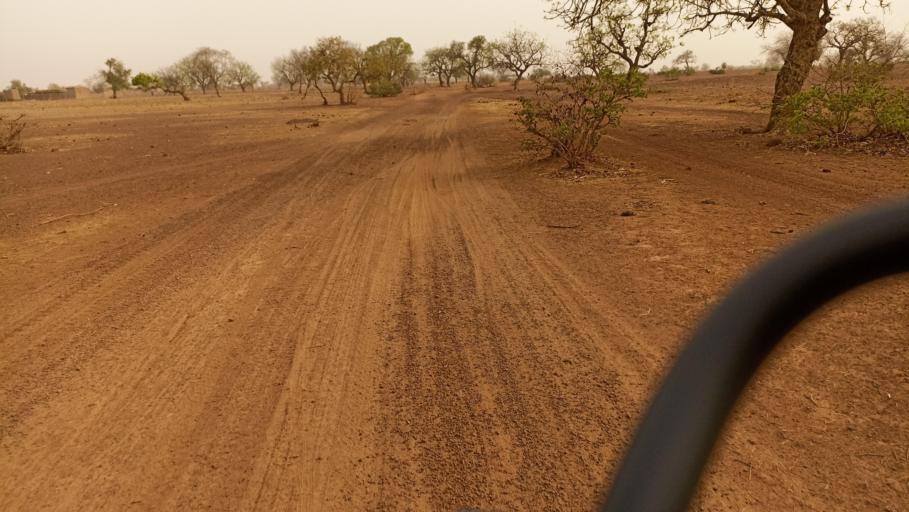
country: BF
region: Nord
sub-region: Province du Zondoma
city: Gourcy
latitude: 13.1470
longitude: -2.5973
